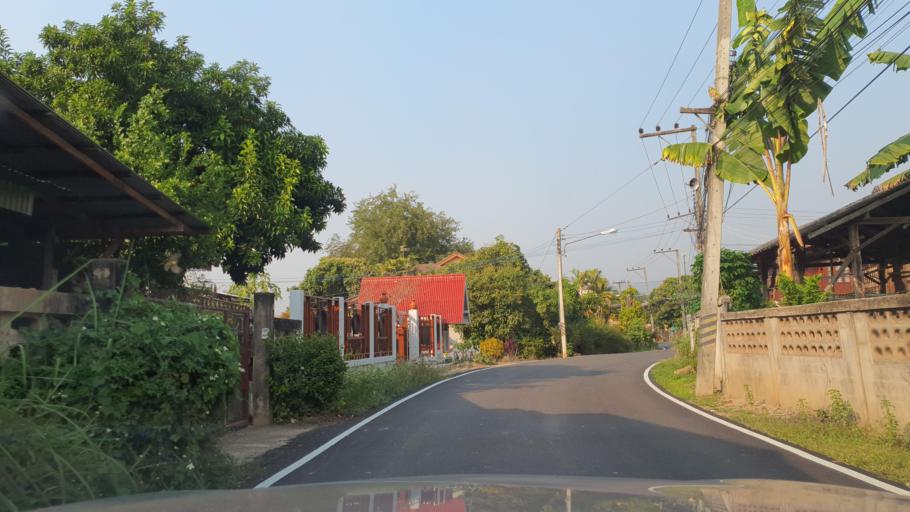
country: TH
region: Chiang Mai
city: Mae Taeng
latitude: 19.1384
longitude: 99.0098
